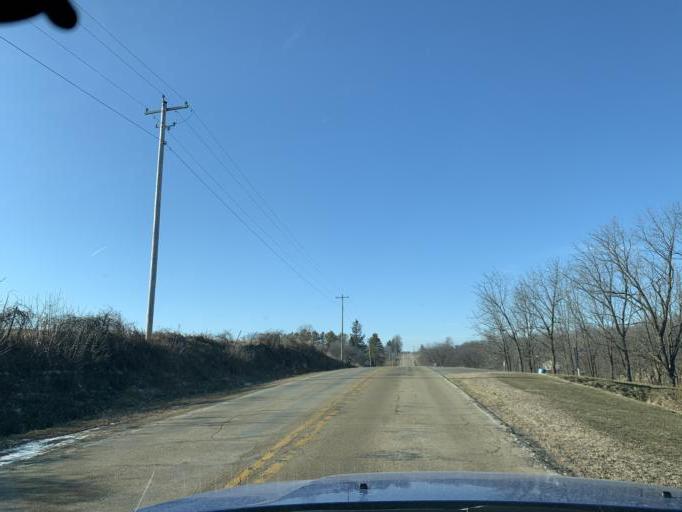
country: US
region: Wisconsin
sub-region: Green County
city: Monroe
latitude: 42.5961
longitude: -89.6068
